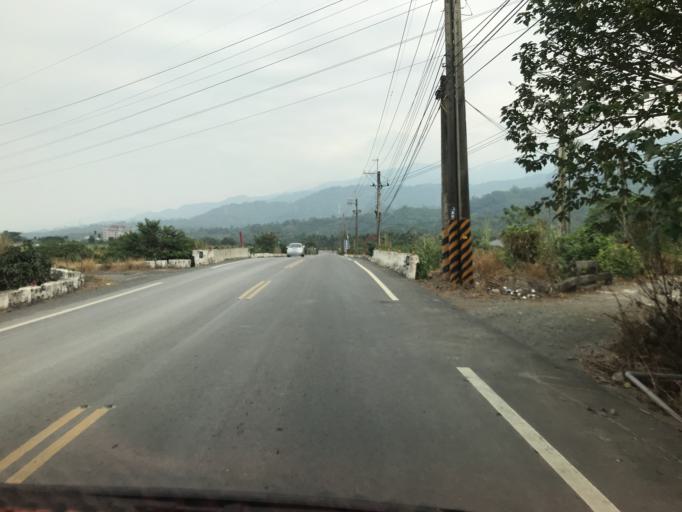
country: TW
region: Taiwan
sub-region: Pingtung
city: Pingtung
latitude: 22.4544
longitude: 120.6119
